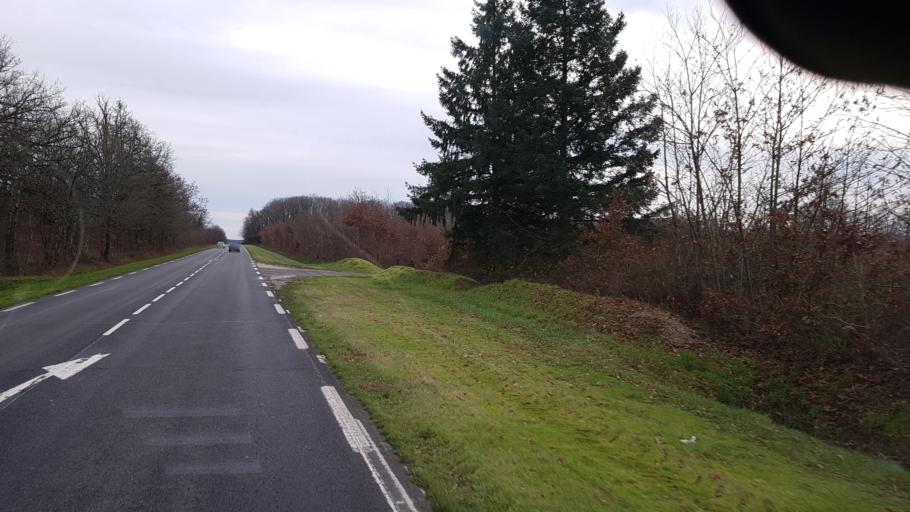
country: FR
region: Centre
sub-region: Departement du Loir-et-Cher
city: Lamotte-Beuvron
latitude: 47.6217
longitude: 2.0122
